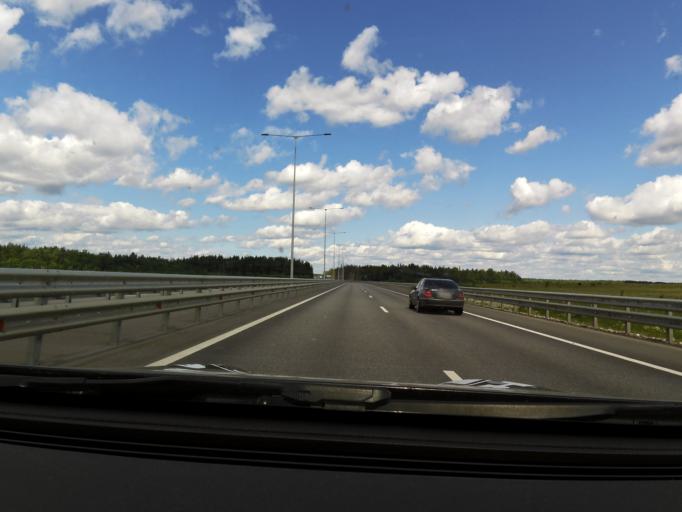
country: RU
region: Tverskaya
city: Vydropuzhsk
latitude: 57.2560
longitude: 34.8814
